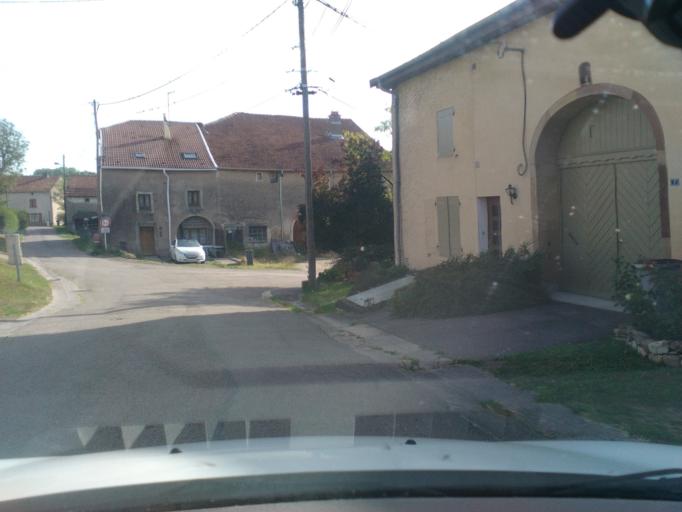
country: FR
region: Lorraine
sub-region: Departement des Vosges
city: Mirecourt
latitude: 48.3088
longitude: 6.0839
